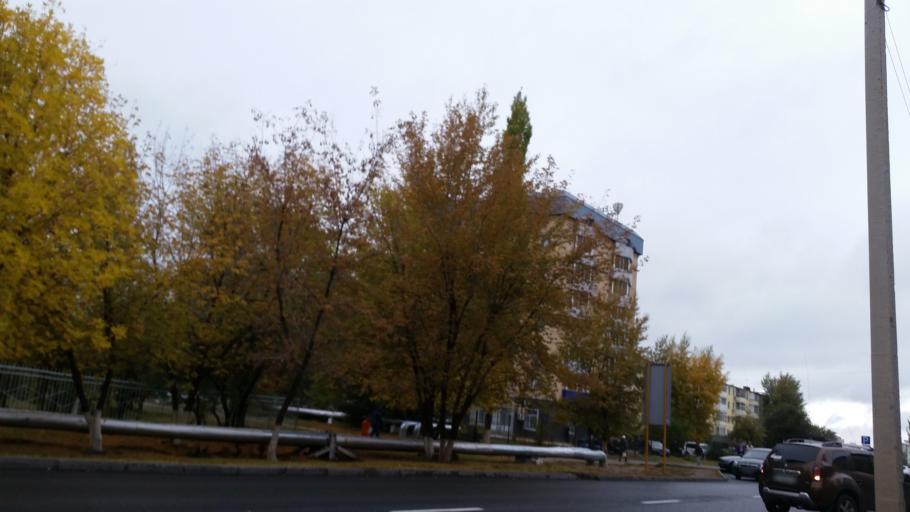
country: KZ
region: Astana Qalasy
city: Astana
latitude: 51.1505
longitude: 71.4627
